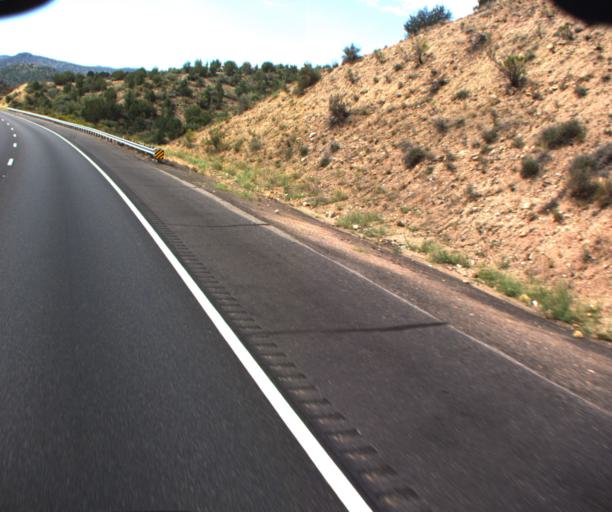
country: US
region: Arizona
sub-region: Yavapai County
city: Camp Verde
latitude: 34.5478
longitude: -111.9097
